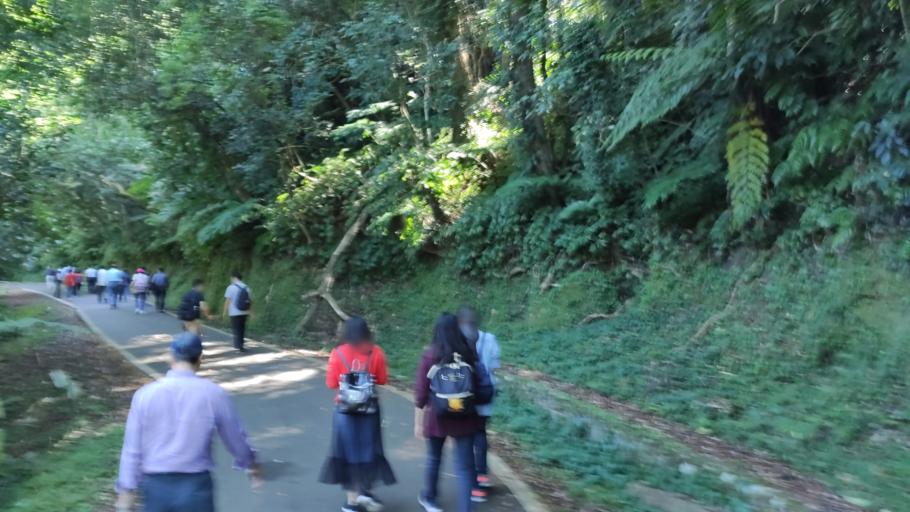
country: TW
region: Taiwan
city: Daxi
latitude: 24.8386
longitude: 121.3066
